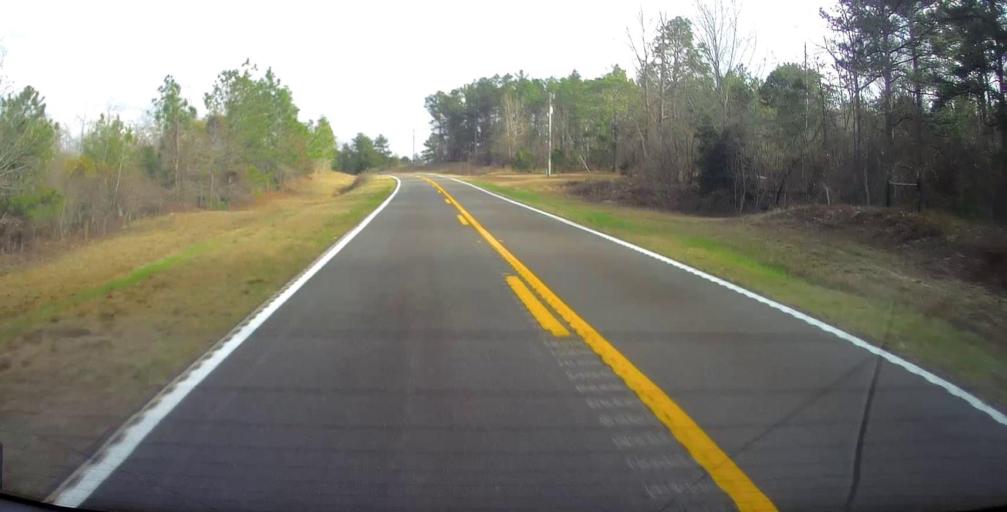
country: US
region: Georgia
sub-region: Marion County
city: Buena Vista
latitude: 32.4388
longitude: -84.5092
